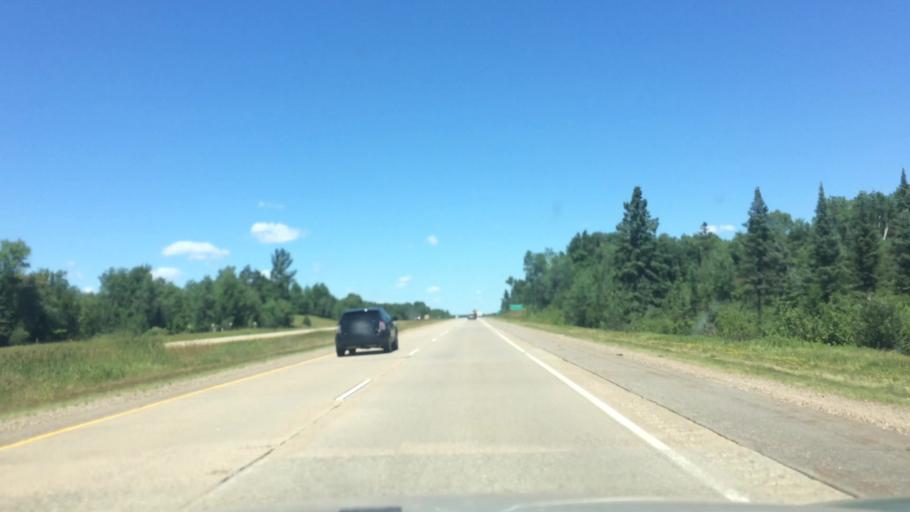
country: US
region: Wisconsin
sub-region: Lincoln County
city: Tomahawk
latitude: 45.3961
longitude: -89.6721
